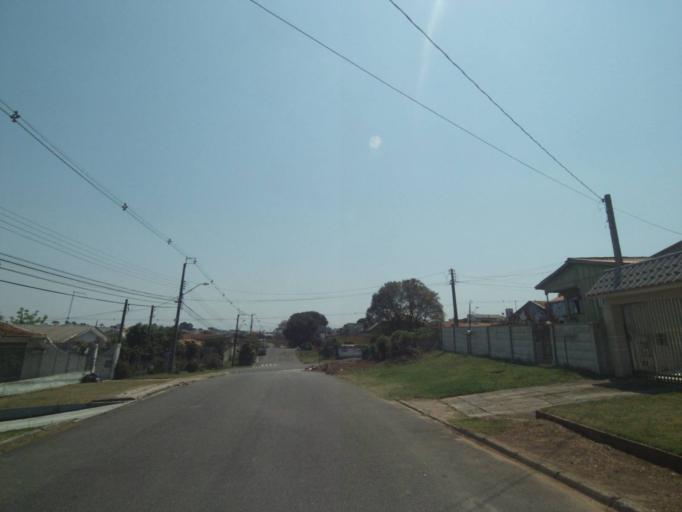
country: BR
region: Parana
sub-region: Sao Jose Dos Pinhais
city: Sao Jose dos Pinhais
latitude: -25.5084
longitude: -49.2674
